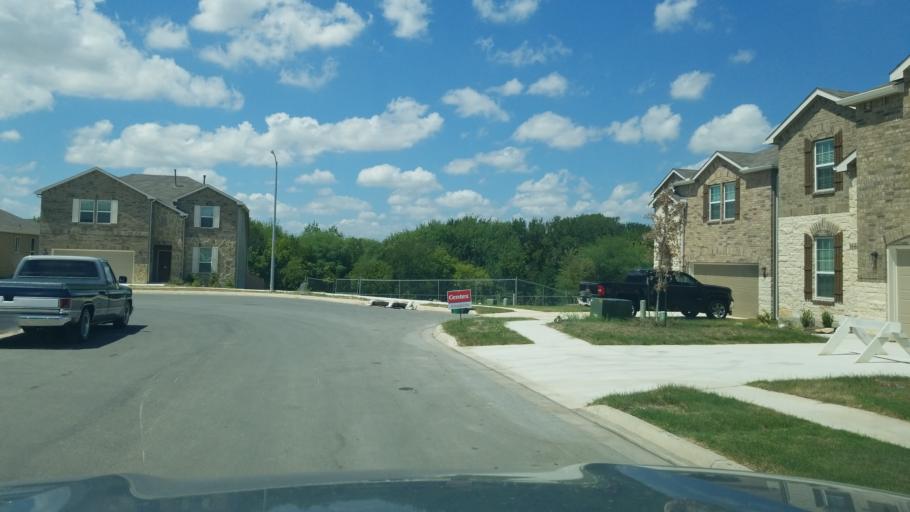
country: US
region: Texas
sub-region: Bexar County
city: Converse
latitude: 29.5355
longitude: -98.3166
